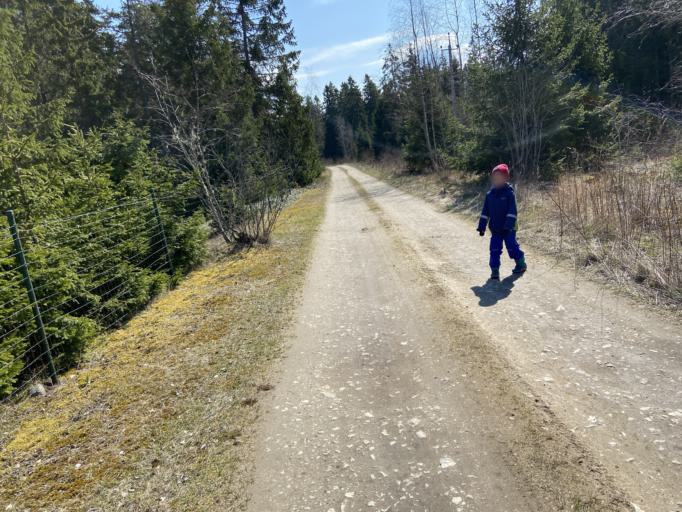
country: EE
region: Harju
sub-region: Kuusalu vald
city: Kuusalu
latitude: 59.6447
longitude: 25.5017
